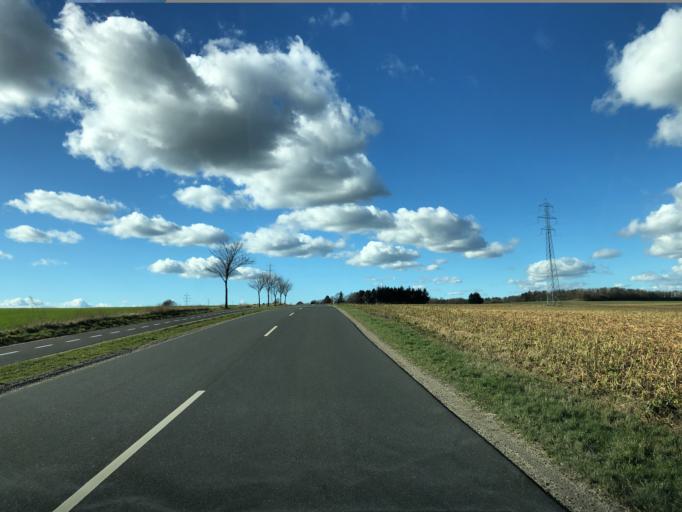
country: DK
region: Central Jutland
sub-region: Favrskov Kommune
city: Hinnerup
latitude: 56.2804
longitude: 10.0340
